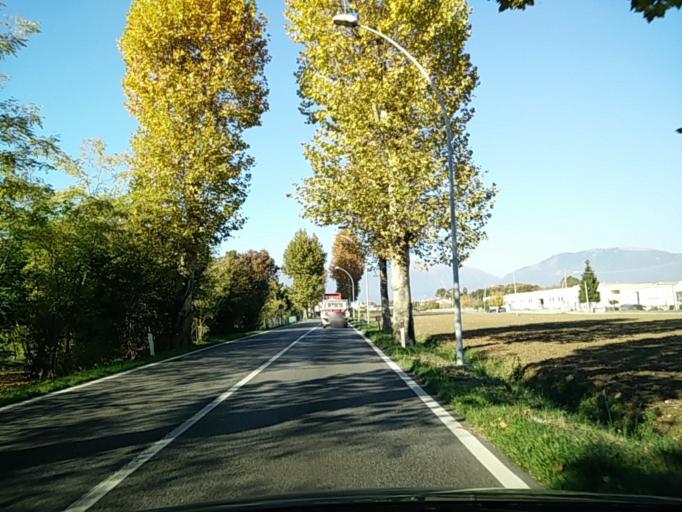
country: IT
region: Veneto
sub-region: Provincia di Treviso
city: San Vendemiano-Fossamerlo
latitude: 45.9041
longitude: 12.3282
